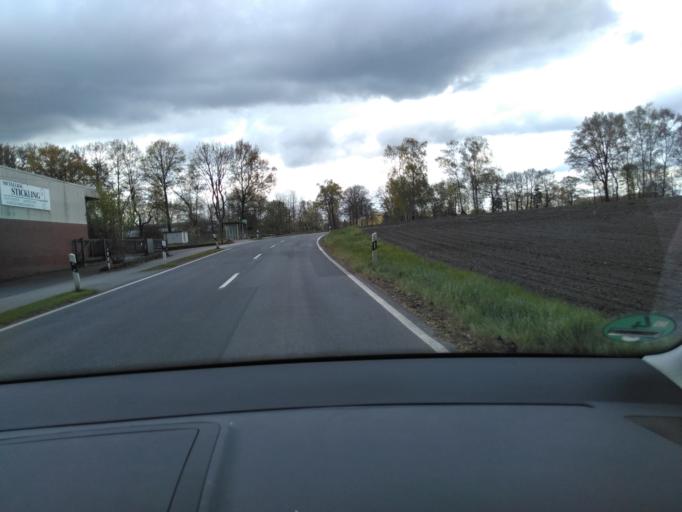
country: DE
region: North Rhine-Westphalia
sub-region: Regierungsbezirk Detmold
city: Verl
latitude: 51.9040
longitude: 8.4657
